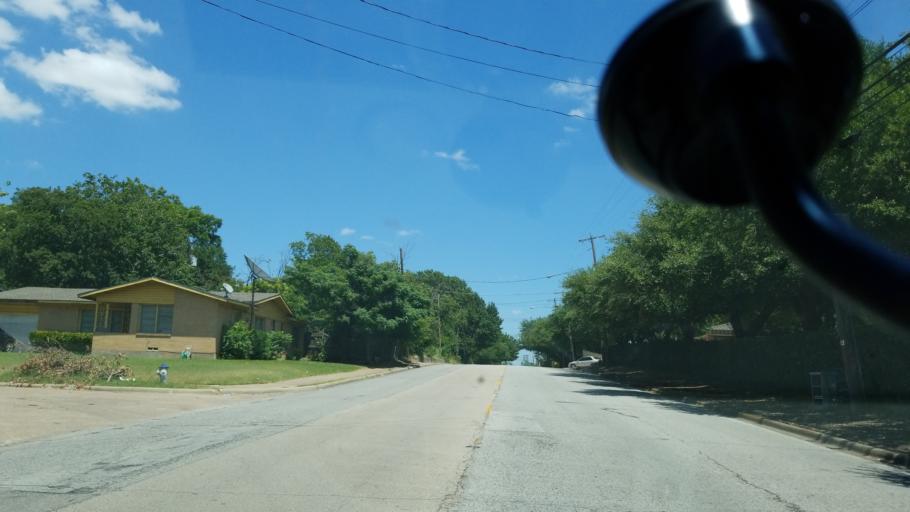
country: US
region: Texas
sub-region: Dallas County
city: Cockrell Hill
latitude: 32.6913
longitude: -96.8174
